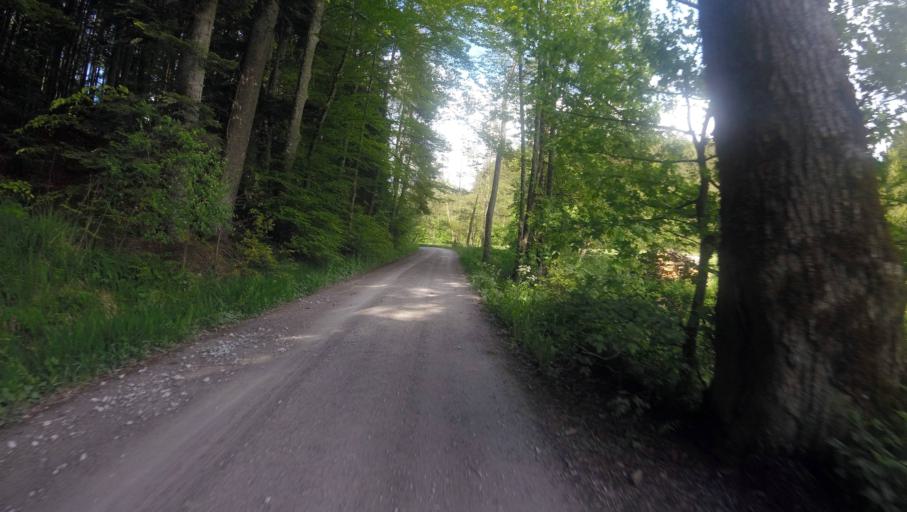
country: DE
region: Baden-Wuerttemberg
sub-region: Regierungsbezirk Stuttgart
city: Alfdorf
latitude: 48.8885
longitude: 9.7017
